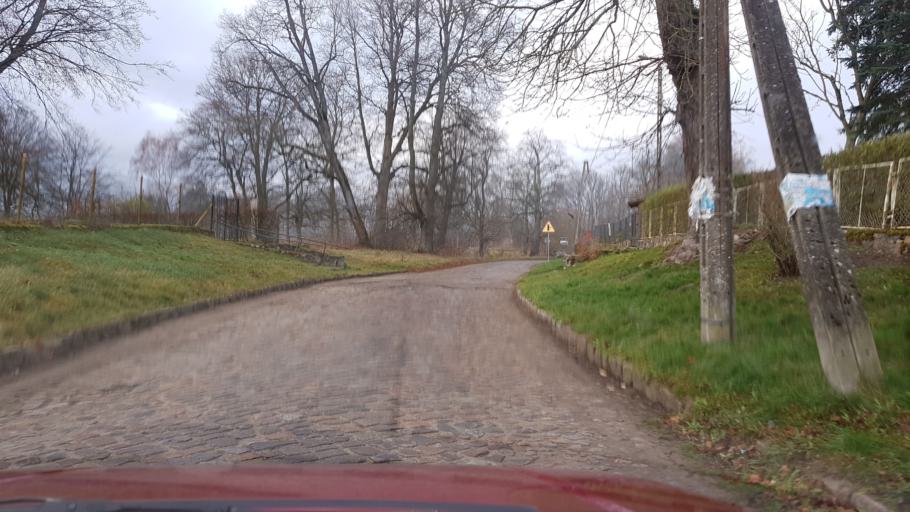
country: PL
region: West Pomeranian Voivodeship
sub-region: Powiat bialogardzki
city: Tychowo
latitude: 53.9802
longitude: 16.3130
